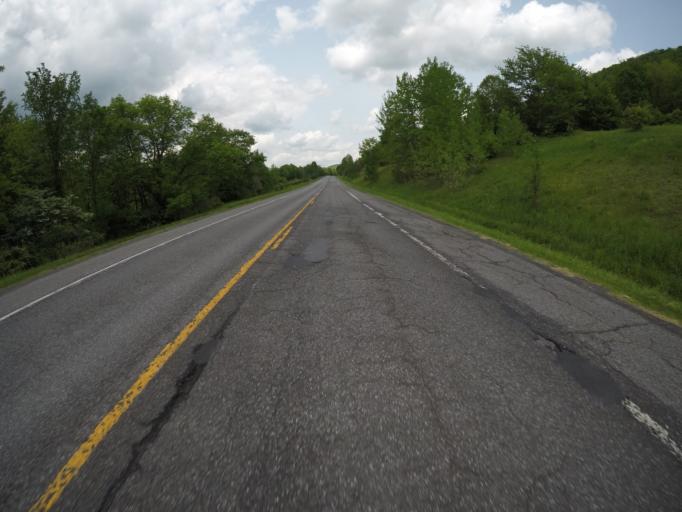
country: US
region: New York
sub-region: Delaware County
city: Stamford
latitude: 42.2556
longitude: -74.5937
